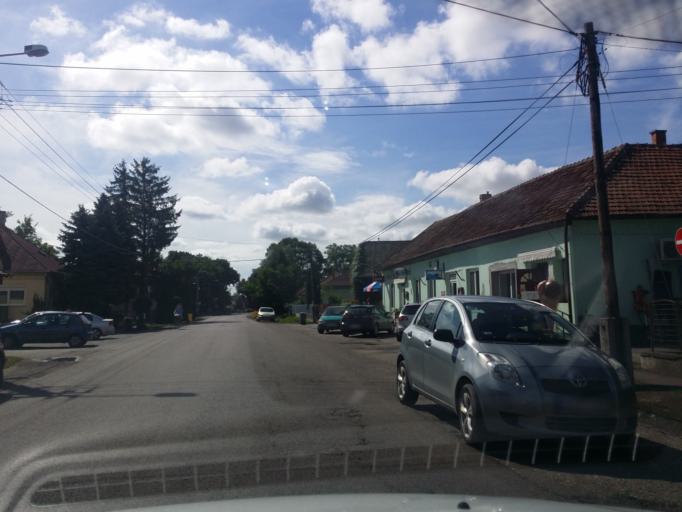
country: HU
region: Jasz-Nagykun-Szolnok
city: Jaszszentandras
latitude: 47.6517
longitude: 20.1543
